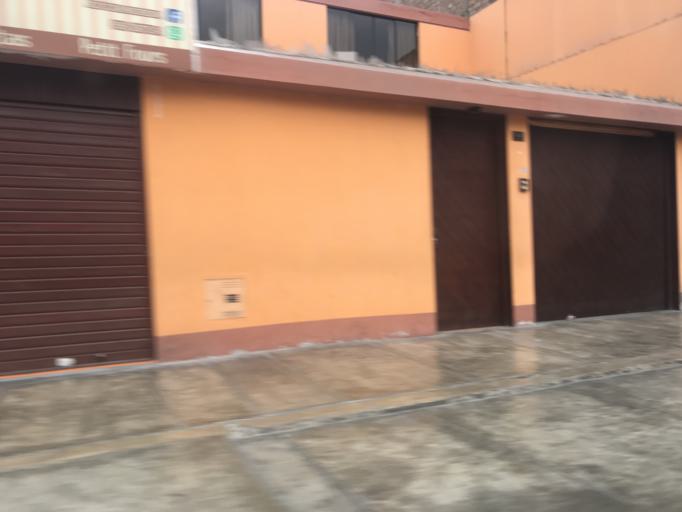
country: PE
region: Callao
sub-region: Callao
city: Callao
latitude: -12.0654
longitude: -77.0959
